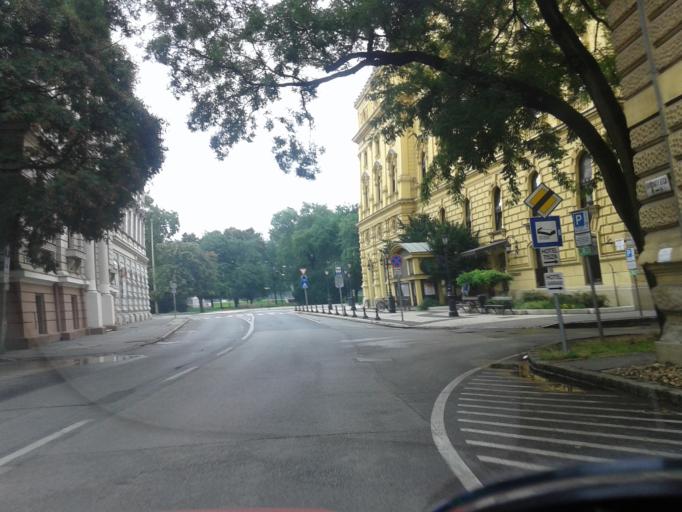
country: HU
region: Csongrad
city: Szeged
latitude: 46.2540
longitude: 20.1515
